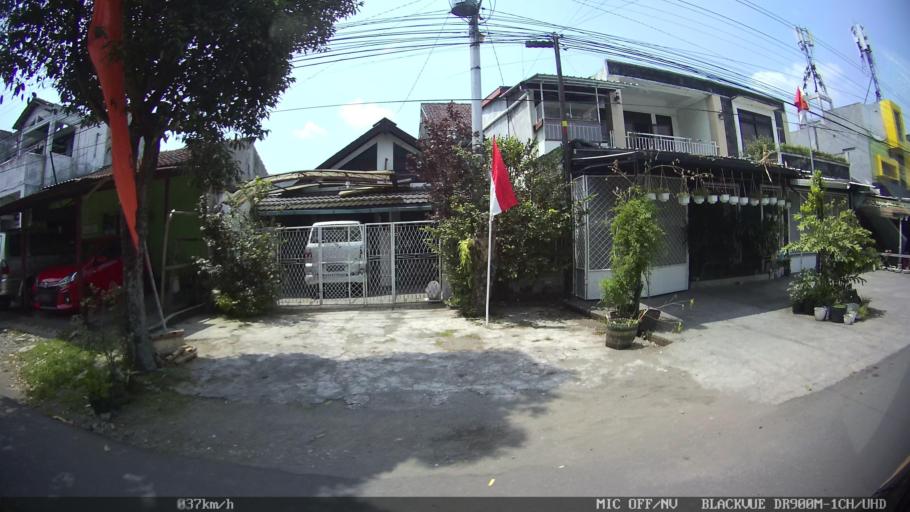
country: ID
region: Daerah Istimewa Yogyakarta
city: Yogyakarta
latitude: -7.8091
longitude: 110.3980
